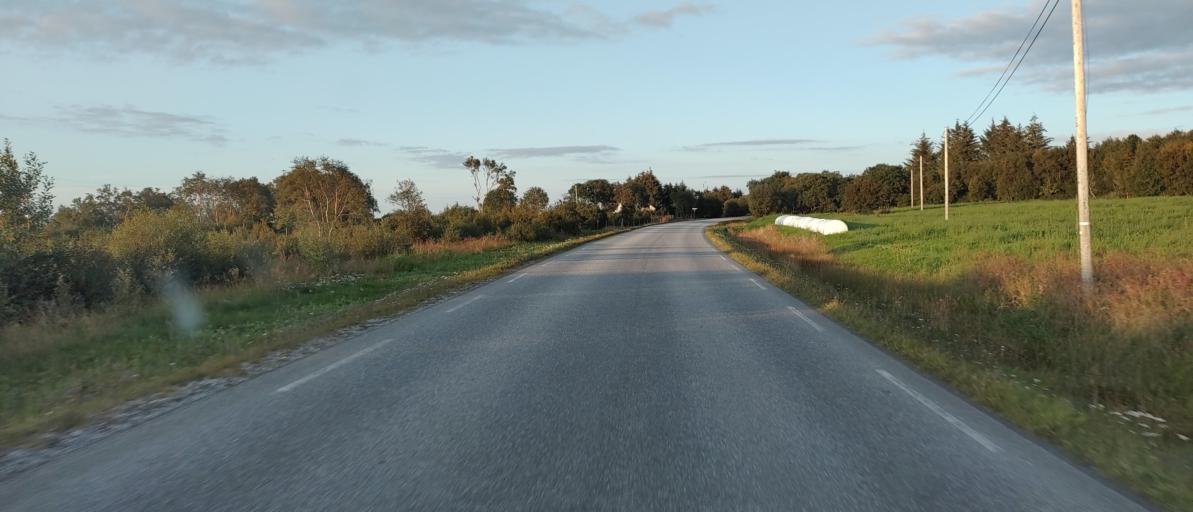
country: NO
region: More og Romsdal
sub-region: Fraena
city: Elnesvagen
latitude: 62.9895
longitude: 7.1701
